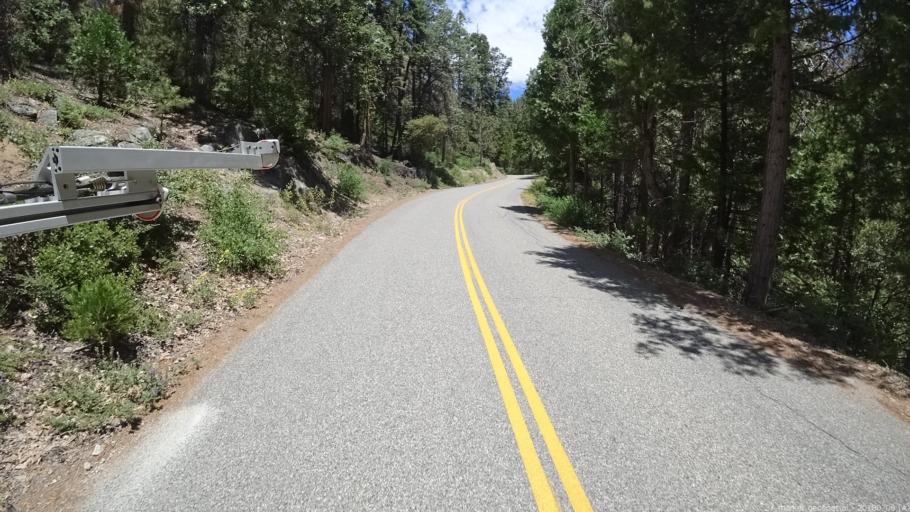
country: US
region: California
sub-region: Madera County
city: Oakhurst
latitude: 37.3758
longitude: -119.5299
